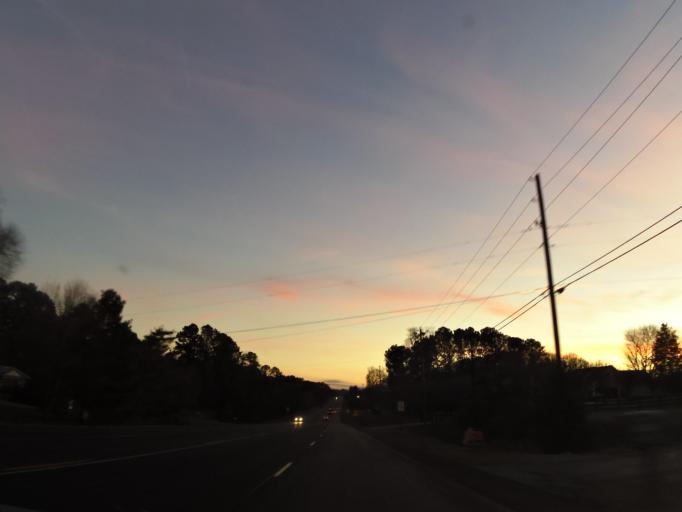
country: US
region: Georgia
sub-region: Whitfield County
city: Varnell
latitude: 34.9542
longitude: -84.9395
